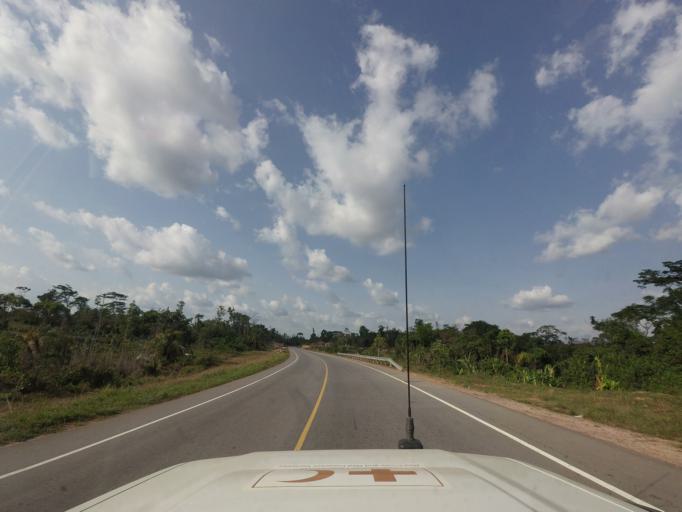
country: LR
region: Bong
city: Gbarnga
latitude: 6.8888
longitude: -9.6619
